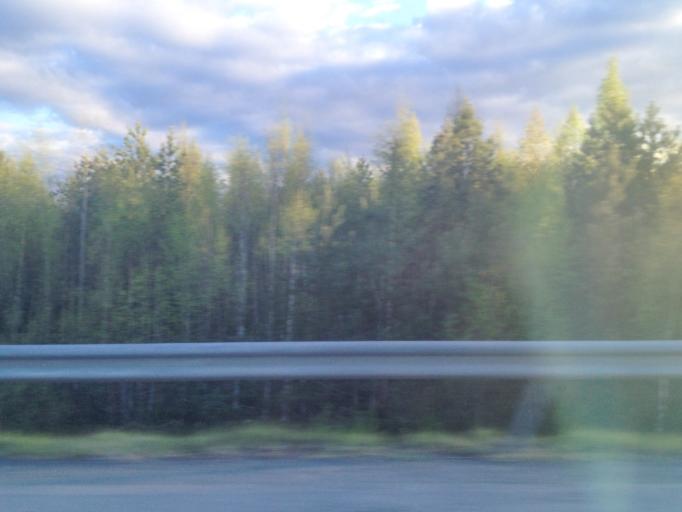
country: FI
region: Haeme
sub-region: Haemeenlinna
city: Kalvola
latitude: 61.1247
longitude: 24.1172
